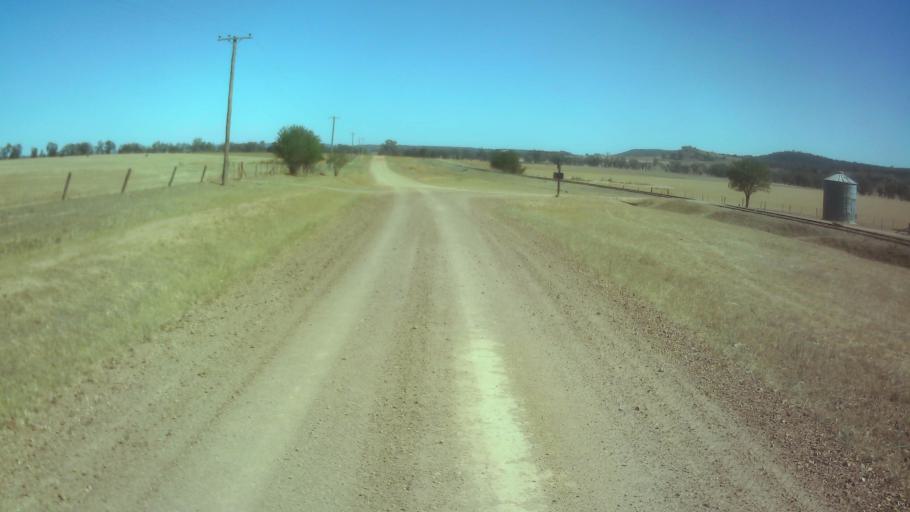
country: AU
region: New South Wales
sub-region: Weddin
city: Grenfell
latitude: -33.9532
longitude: 148.3011
